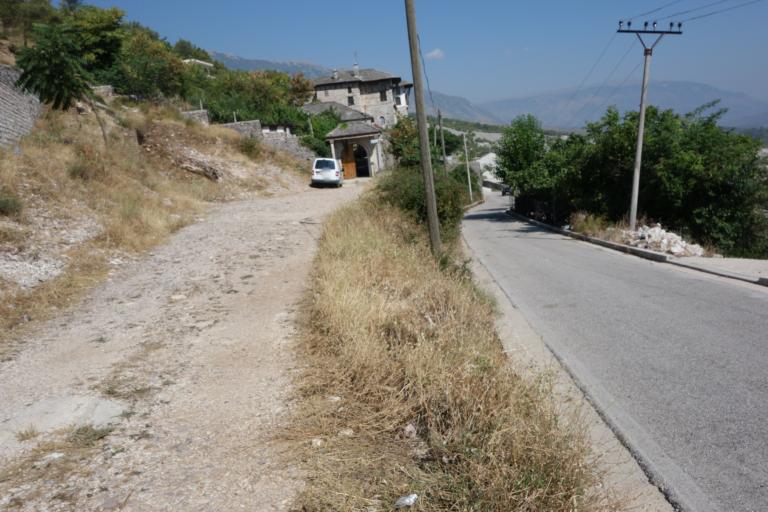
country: AL
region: Gjirokaster
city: Gjirokaster
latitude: 40.0743
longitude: 20.1332
